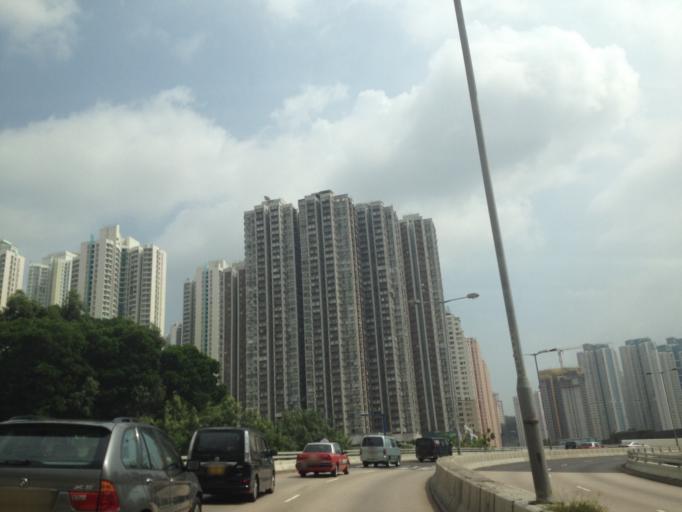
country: HK
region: Kowloon City
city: Kowloon
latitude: 22.3287
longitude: 114.2124
